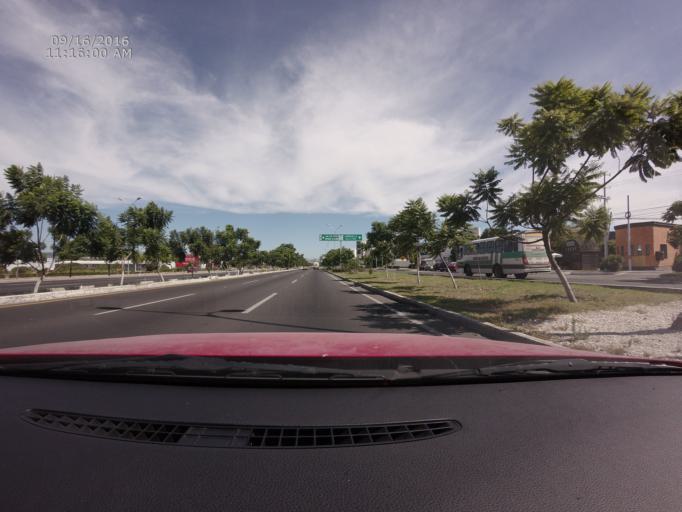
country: MX
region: Queretaro
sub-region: Queretaro
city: El Salitre
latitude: 20.6552
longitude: -100.4320
